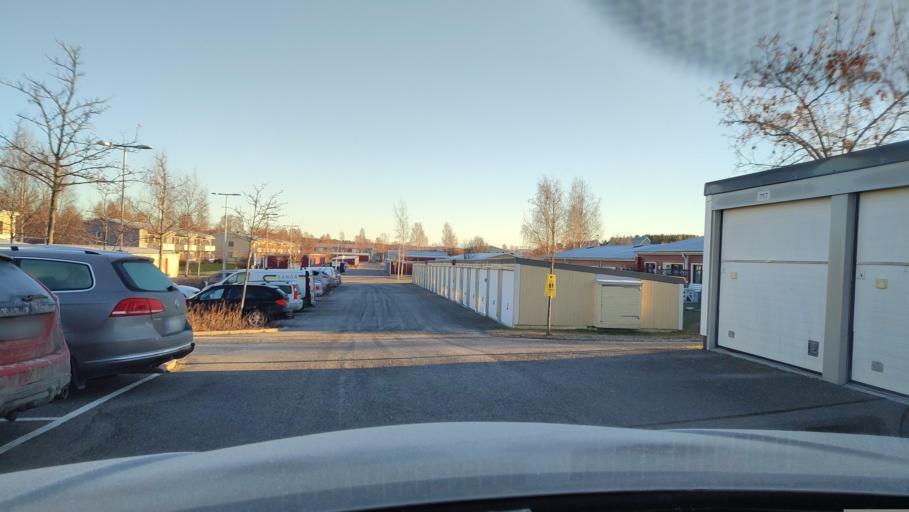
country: SE
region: Vaesterbotten
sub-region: Skelleftea Kommun
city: Skelleftea
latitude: 64.7434
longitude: 20.9811
